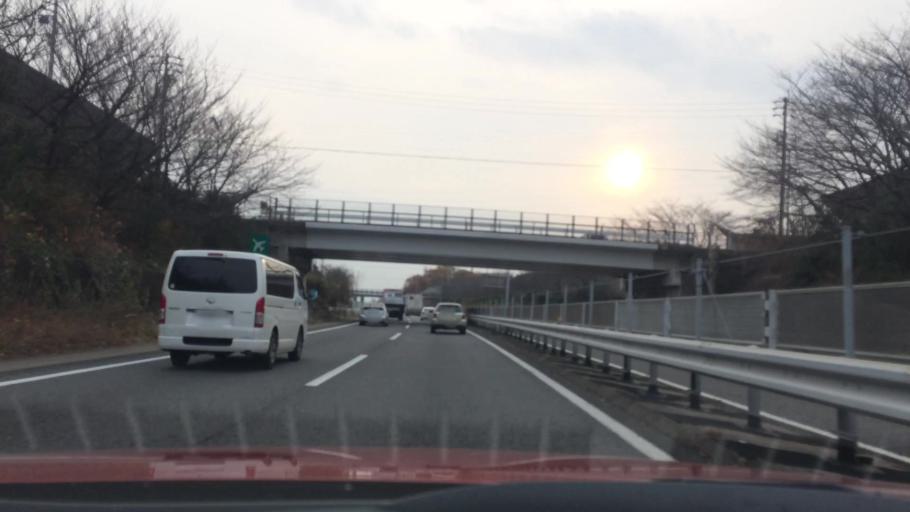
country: JP
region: Aichi
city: Kasugai
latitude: 35.2925
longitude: 136.9842
